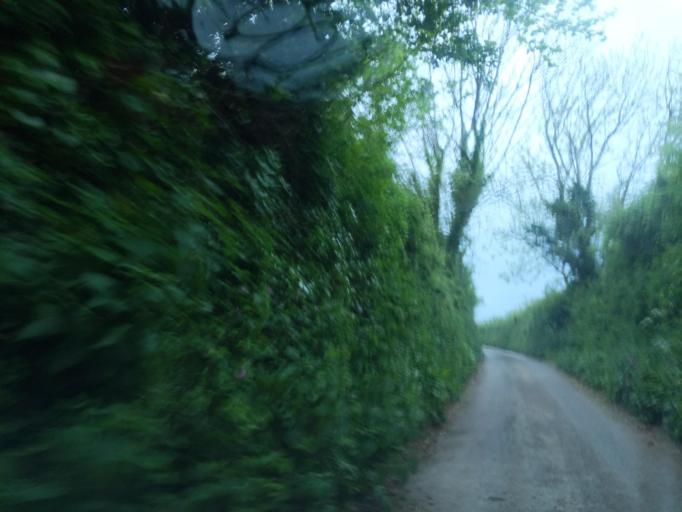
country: GB
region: England
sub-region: Borough of Torbay
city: Brixham
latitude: 50.3634
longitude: -3.5303
